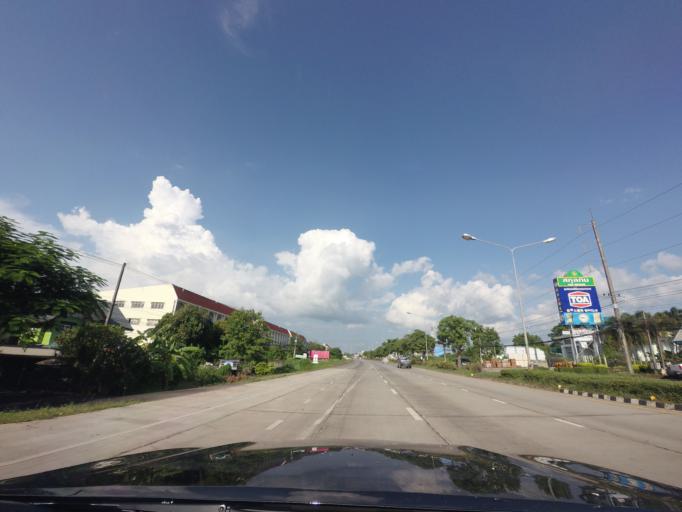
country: TH
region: Nong Khai
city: Nong Khai
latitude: 17.8812
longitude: 102.7528
